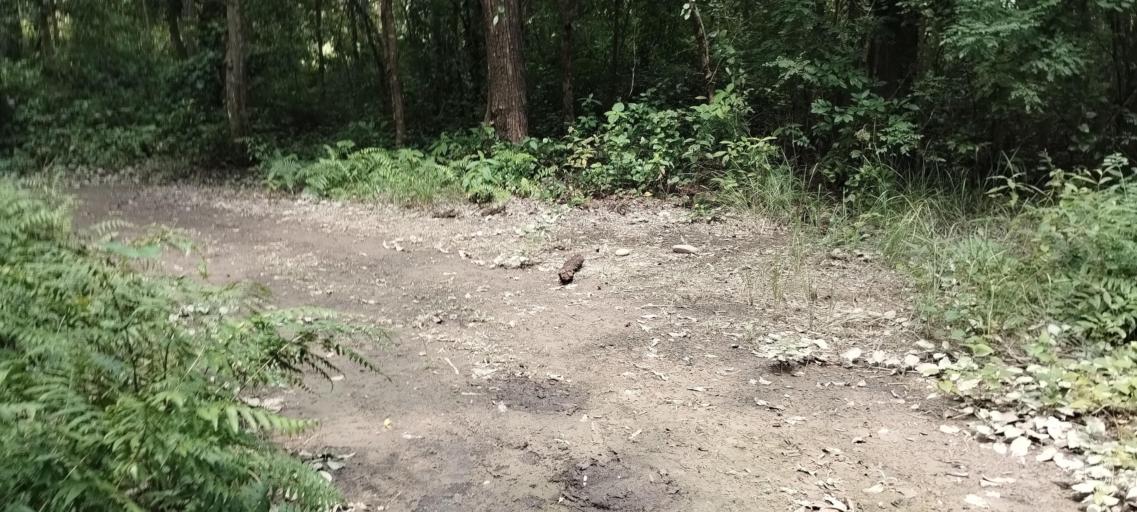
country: NP
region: Far Western
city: Tikapur
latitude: 28.4852
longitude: 81.2510
